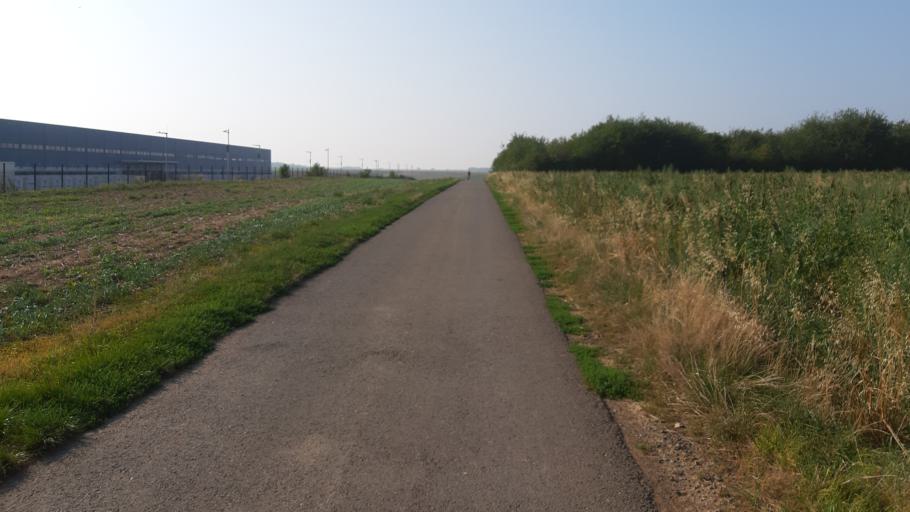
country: DE
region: Rheinland-Pfalz
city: Gau-Bischofsheim
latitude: 49.9418
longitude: 8.2517
